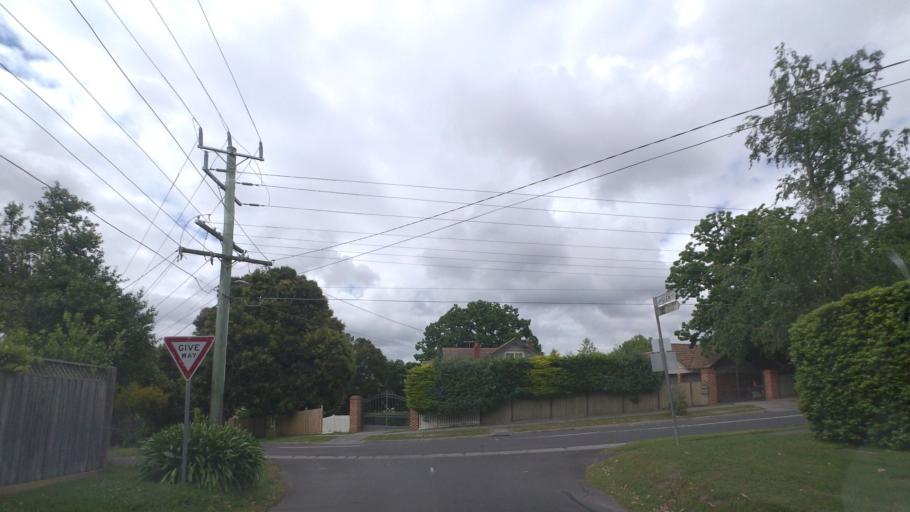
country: AU
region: Victoria
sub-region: Maroondah
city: Croydon South
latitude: -37.7945
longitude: 145.2759
